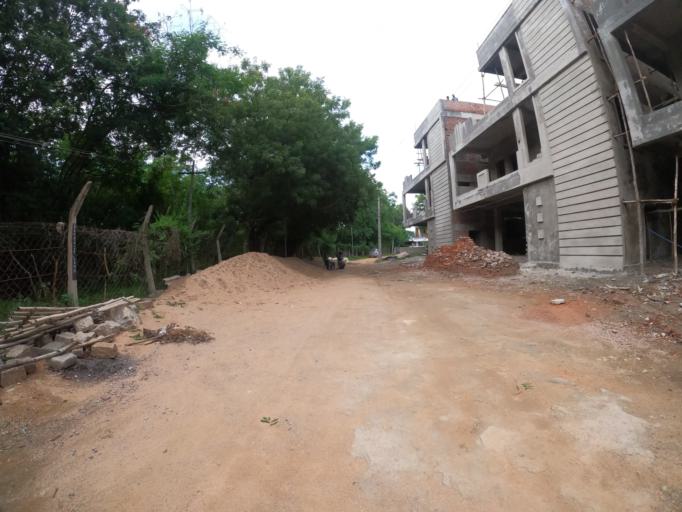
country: IN
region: Telangana
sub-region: Hyderabad
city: Hyderabad
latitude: 17.3542
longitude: 78.3903
